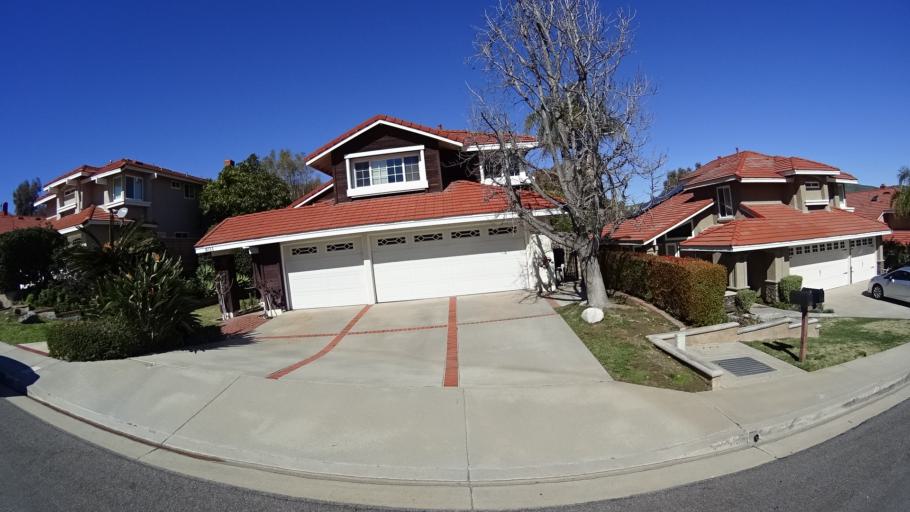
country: US
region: California
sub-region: Orange County
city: Yorba Linda
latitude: 33.8632
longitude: -117.7469
